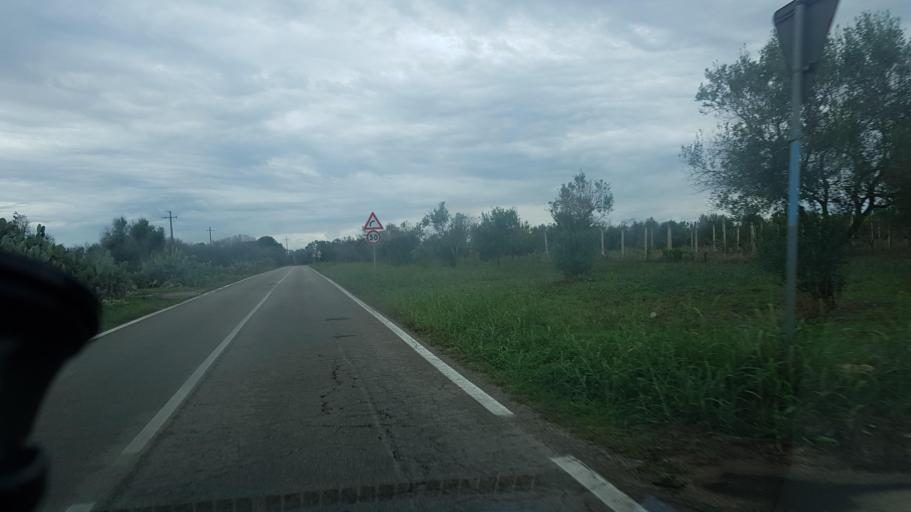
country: IT
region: Apulia
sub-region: Provincia di Lecce
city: Salice Salentino
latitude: 40.3691
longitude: 17.9900
